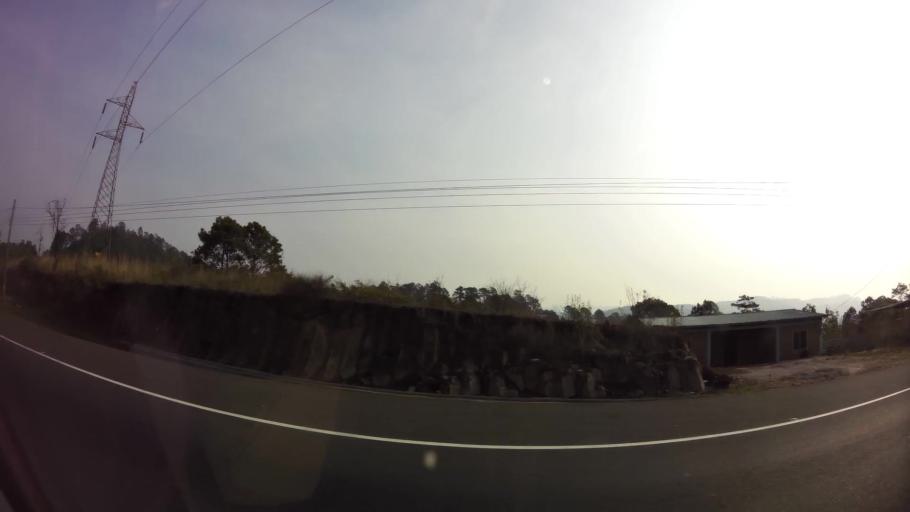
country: HN
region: Francisco Morazan
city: Zambrano
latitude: 14.2657
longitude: -87.3959
